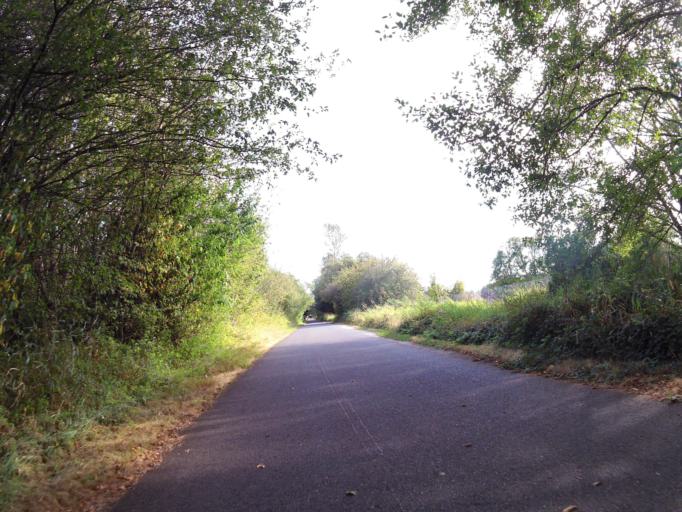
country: US
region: Washington
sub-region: Thurston County
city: Lacey
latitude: 47.0166
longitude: -122.8339
